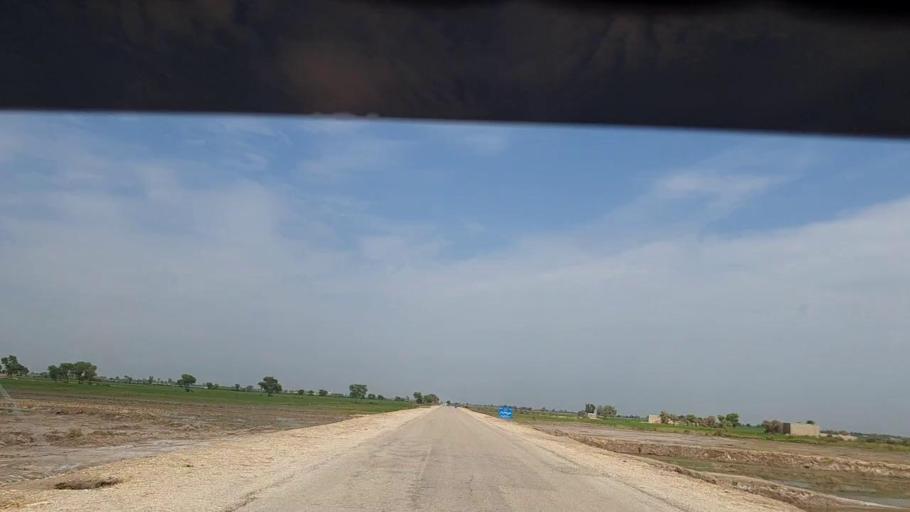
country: PK
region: Sindh
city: Thul
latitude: 28.1920
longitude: 68.7682
